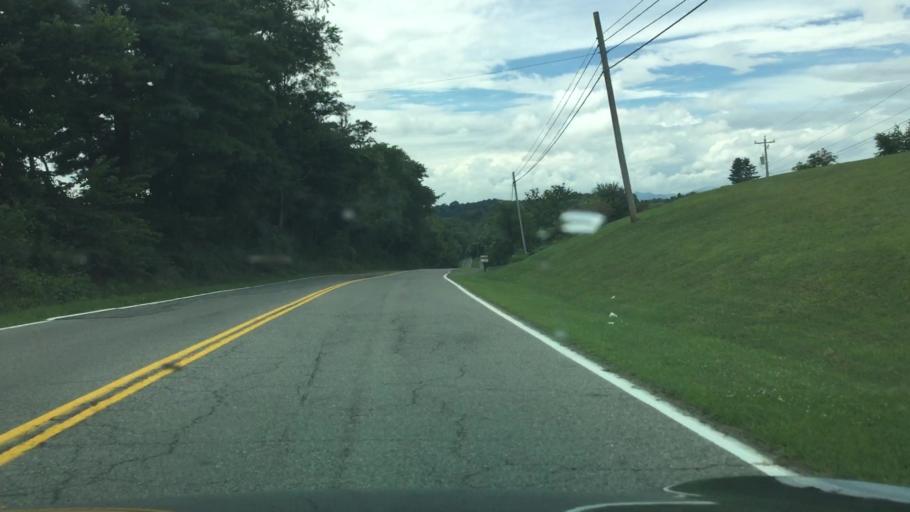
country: US
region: Virginia
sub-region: Pulaski County
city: Pulaski
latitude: 36.9493
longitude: -80.8946
